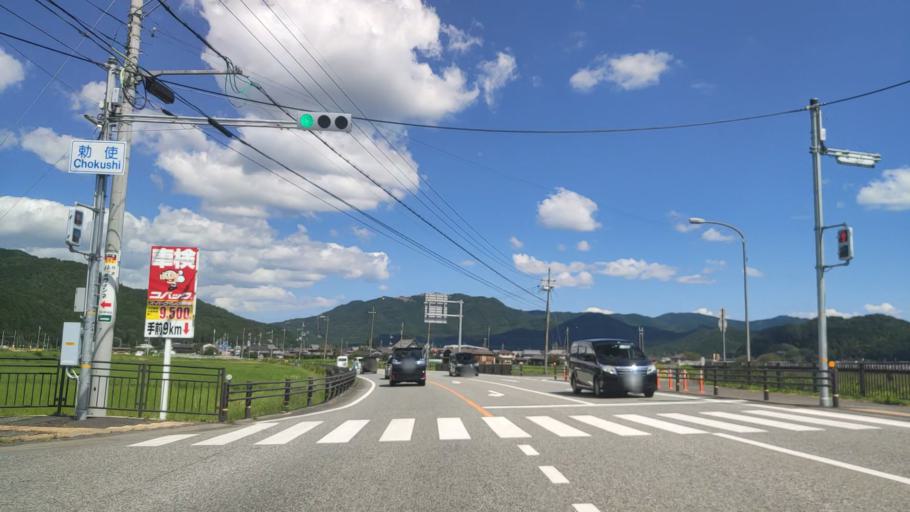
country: JP
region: Kyoto
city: Fukuchiyama
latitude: 35.1945
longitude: 135.1211
